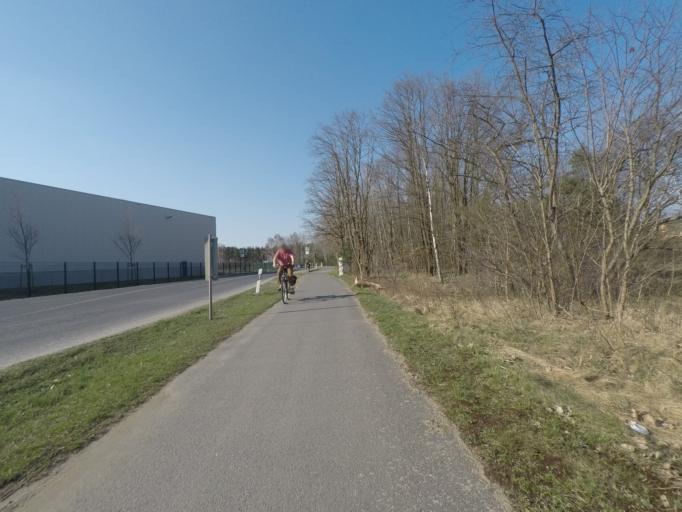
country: DE
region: Brandenburg
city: Eberswalde
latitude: 52.8509
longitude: 13.7737
